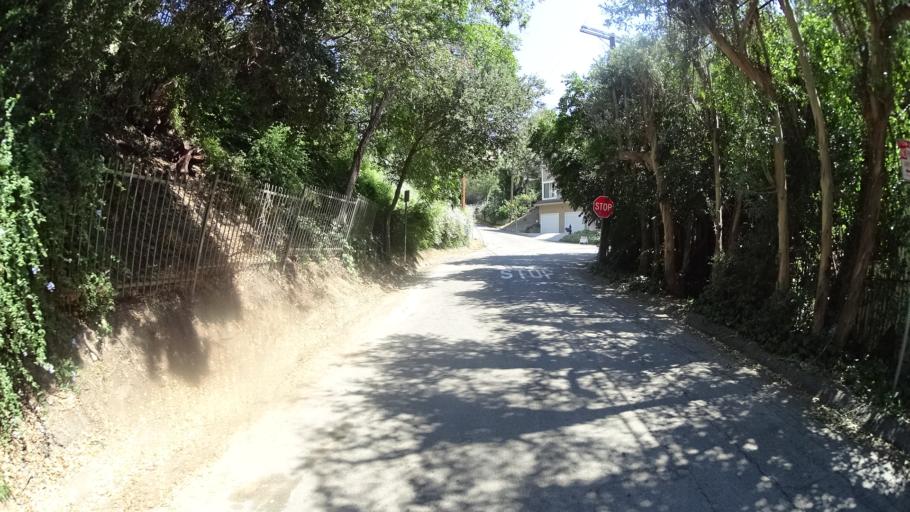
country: US
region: California
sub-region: Los Angeles County
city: North Hollywood
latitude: 34.1411
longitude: -118.4059
